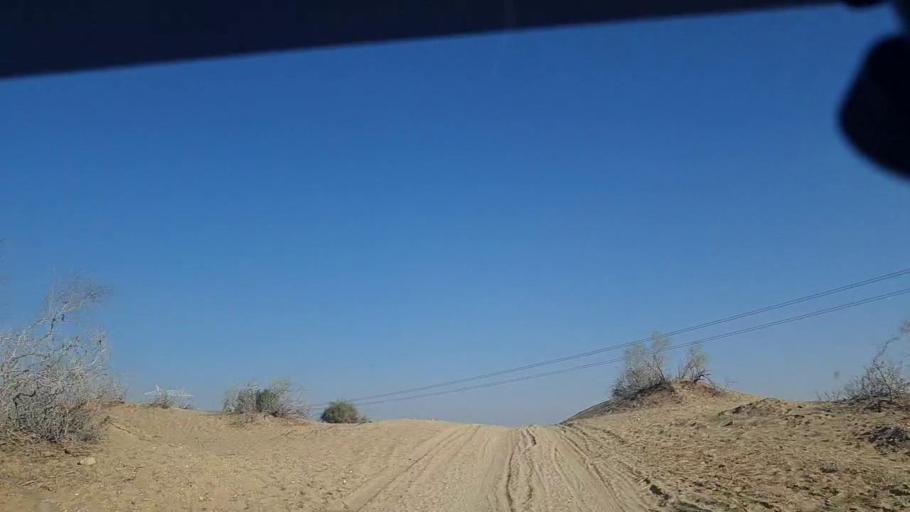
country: PK
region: Sindh
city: Khanpur
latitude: 27.6451
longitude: 69.4037
